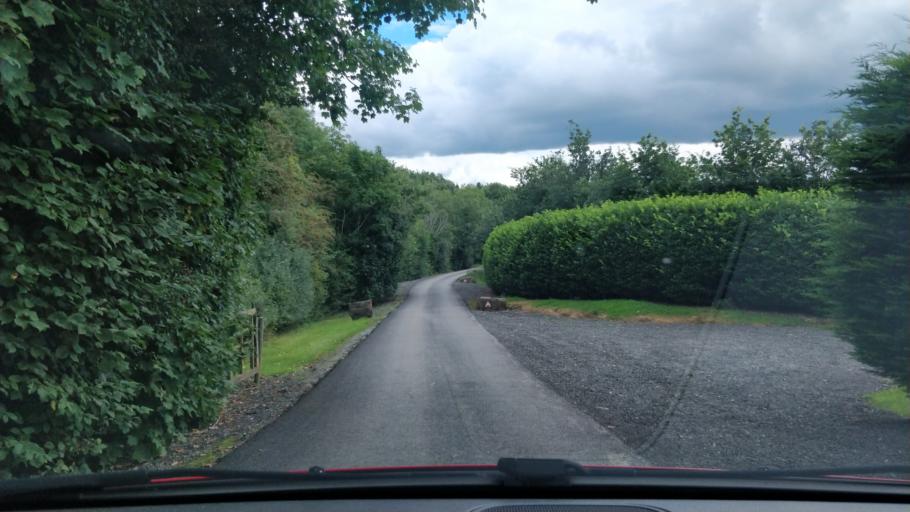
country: GB
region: Wales
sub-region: Wrexham
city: Rossett
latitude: 53.1512
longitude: -2.9374
